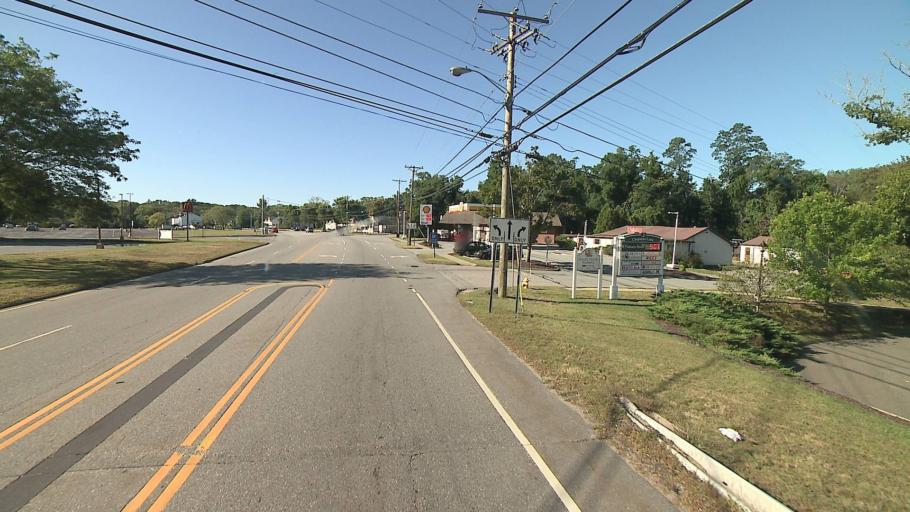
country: US
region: Connecticut
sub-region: New London County
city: Gales Ferry
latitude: 41.4307
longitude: -72.0820
